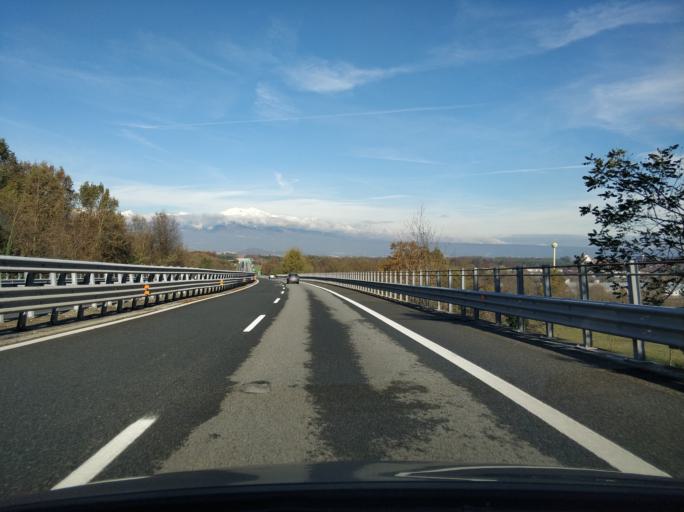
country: IT
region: Piedmont
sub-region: Provincia di Torino
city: Scarmagno
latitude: 45.3742
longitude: 7.8443
